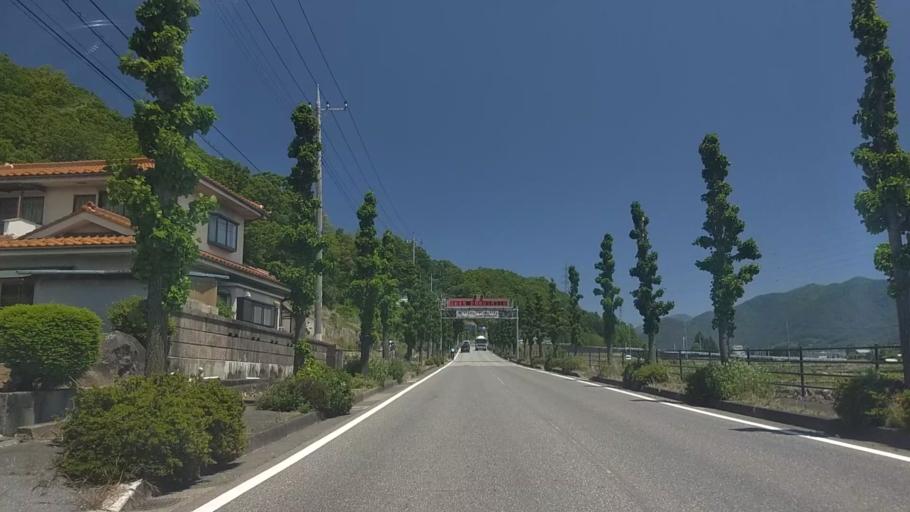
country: JP
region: Yamanashi
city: Nirasaki
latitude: 35.7985
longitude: 138.4248
